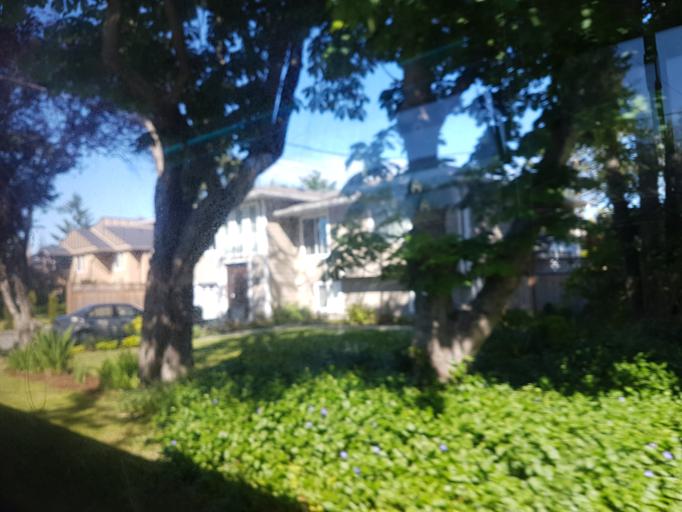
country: CA
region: British Columbia
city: Oak Bay
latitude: 48.4848
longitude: -123.3331
